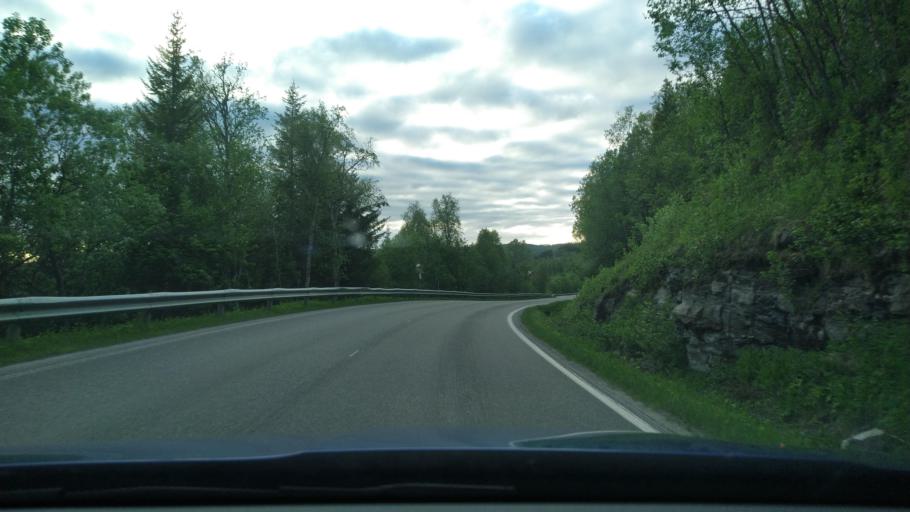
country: NO
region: Troms
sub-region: Sorreisa
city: Sorreisa
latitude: 69.0838
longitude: 18.3593
